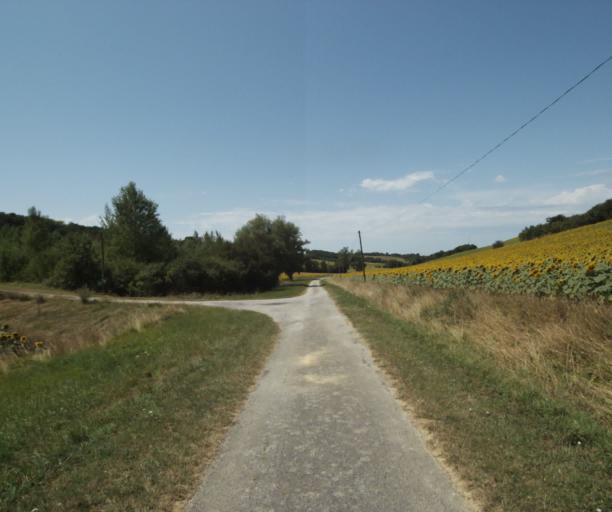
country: FR
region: Midi-Pyrenees
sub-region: Departement de la Haute-Garonne
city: Saint-Felix-Lauragais
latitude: 43.4458
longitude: 1.8689
